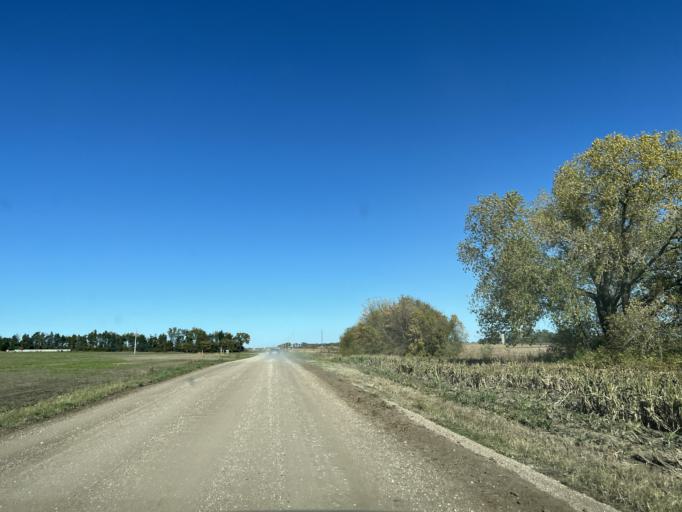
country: US
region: Kansas
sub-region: McPherson County
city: Moundridge
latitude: 38.2159
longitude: -97.6292
